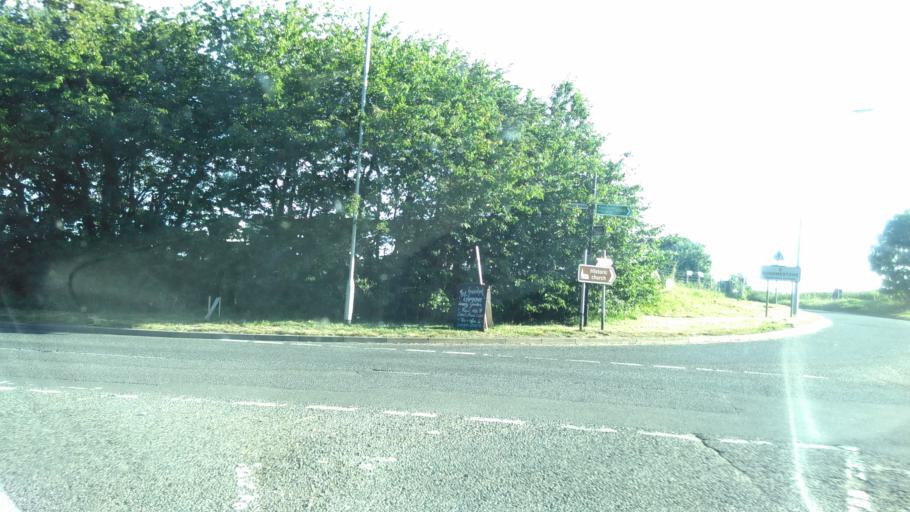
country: GB
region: England
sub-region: Kent
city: Faversham
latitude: 51.3102
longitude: 0.9321
